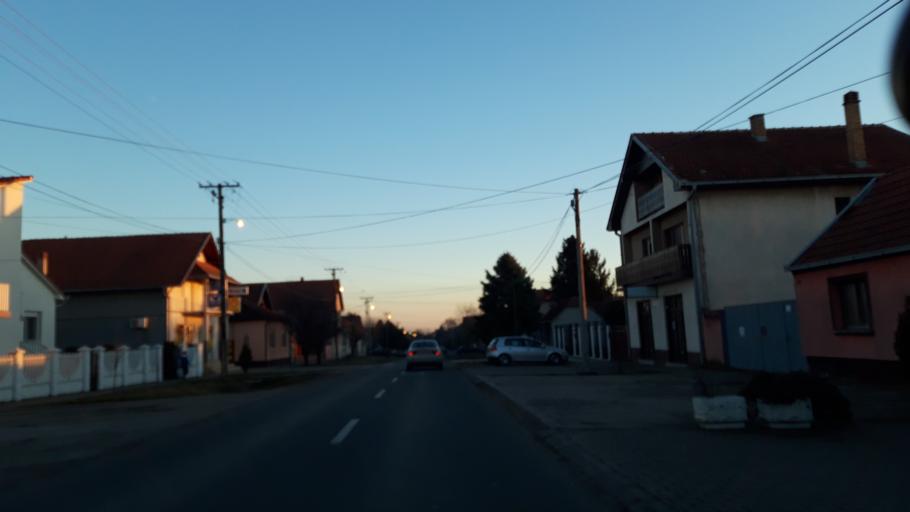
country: RS
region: Autonomna Pokrajina Vojvodina
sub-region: Sremski Okrug
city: Ingija
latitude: 45.0415
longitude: 20.0782
